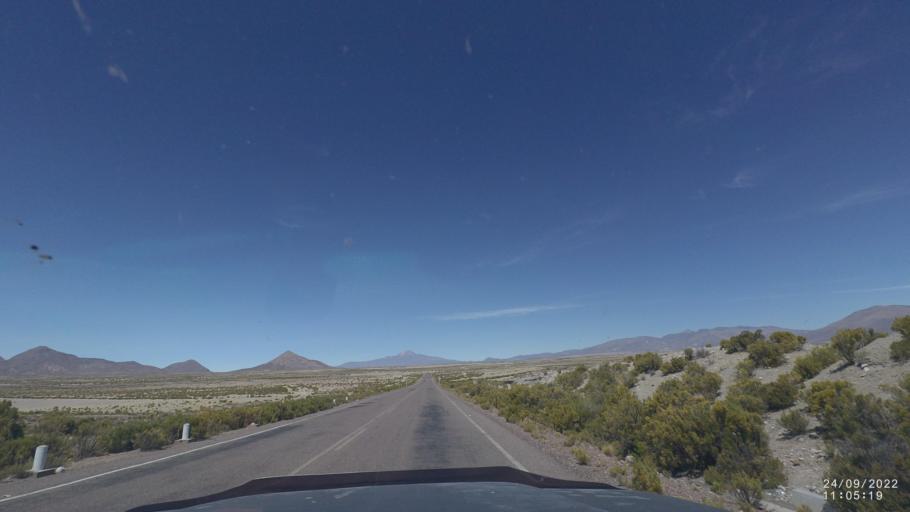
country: BO
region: Oruro
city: Challapata
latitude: -19.4727
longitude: -67.4289
